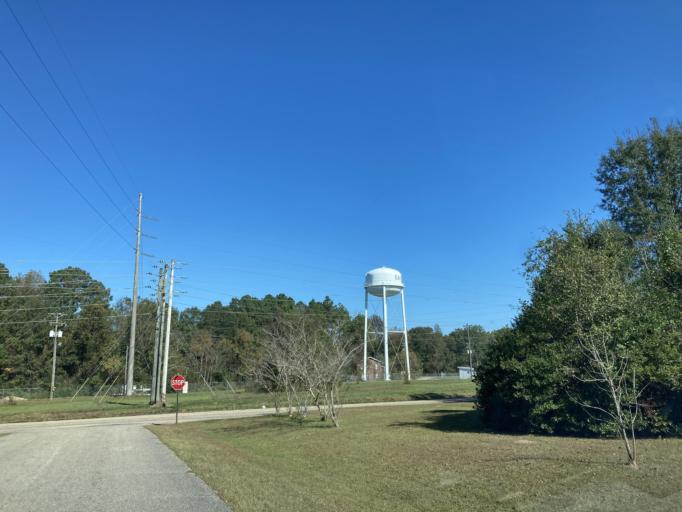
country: US
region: Mississippi
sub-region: Lamar County
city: West Hattiesburg
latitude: 31.2708
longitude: -89.4146
